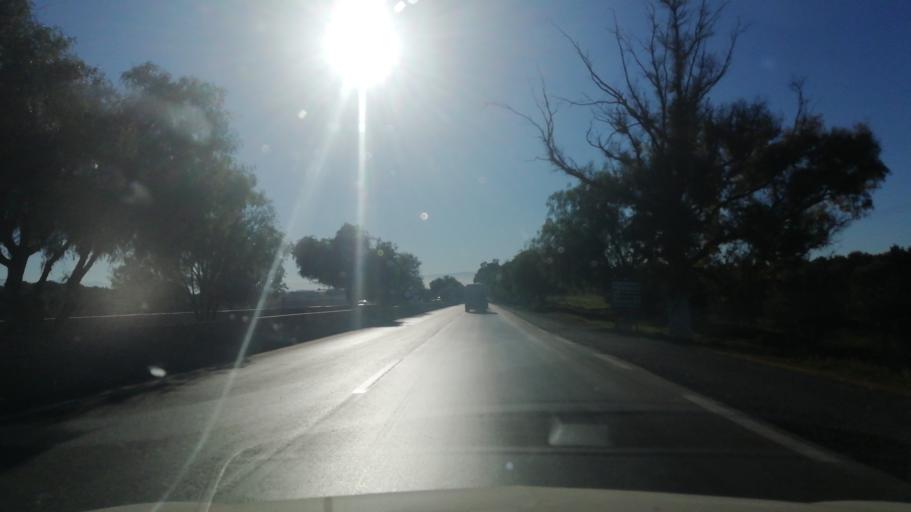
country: DZ
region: Tlemcen
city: Remchi
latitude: 35.0248
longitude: -1.4004
